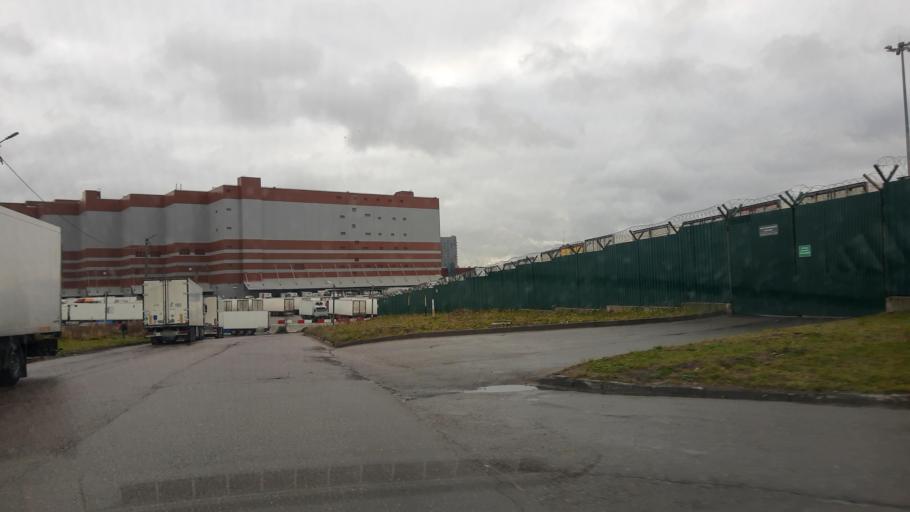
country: RU
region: Moskovskaya
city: Mosrentgen
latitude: 55.6006
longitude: 37.4554
